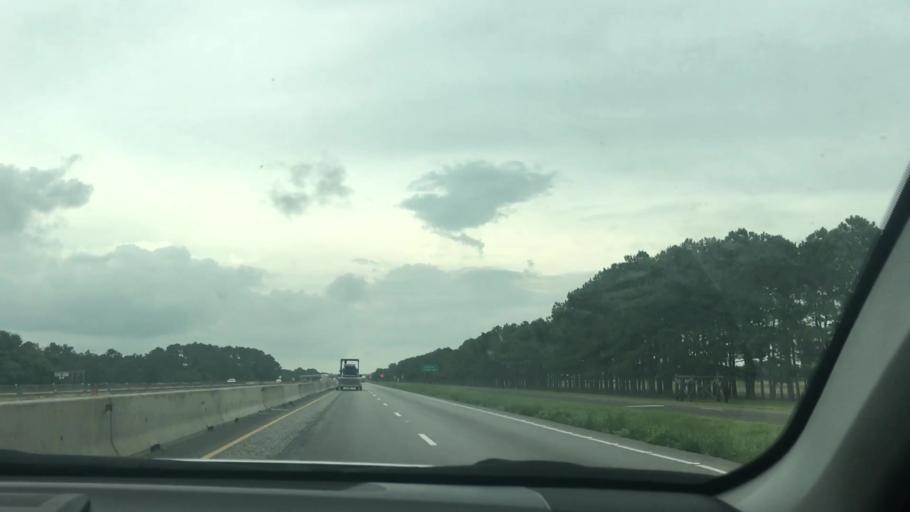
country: US
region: Texas
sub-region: Chambers County
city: Winnie
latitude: 29.8573
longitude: -94.3583
